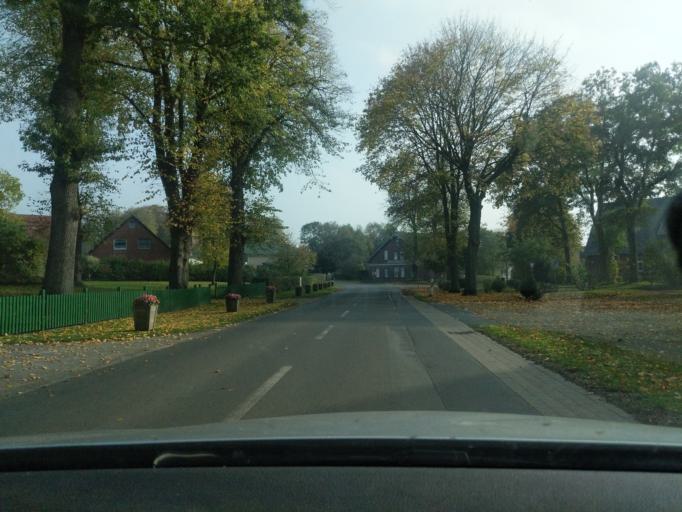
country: DE
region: Lower Saxony
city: Wanna
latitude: 53.7422
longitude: 8.7786
